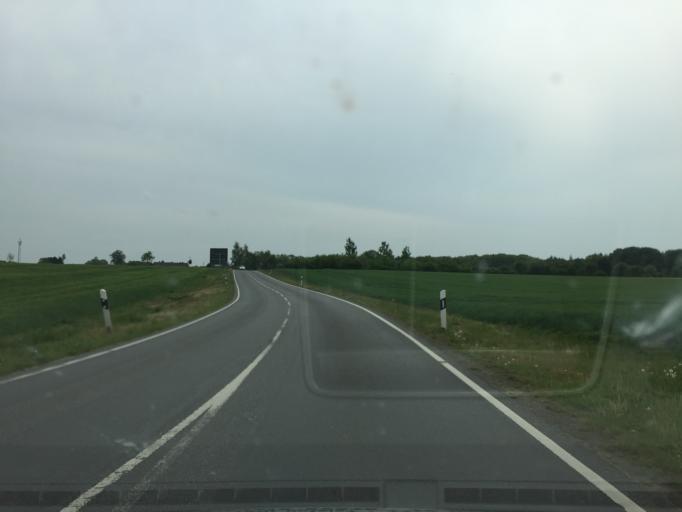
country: DE
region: Lower Saxony
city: Syke
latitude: 52.9118
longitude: 8.7927
